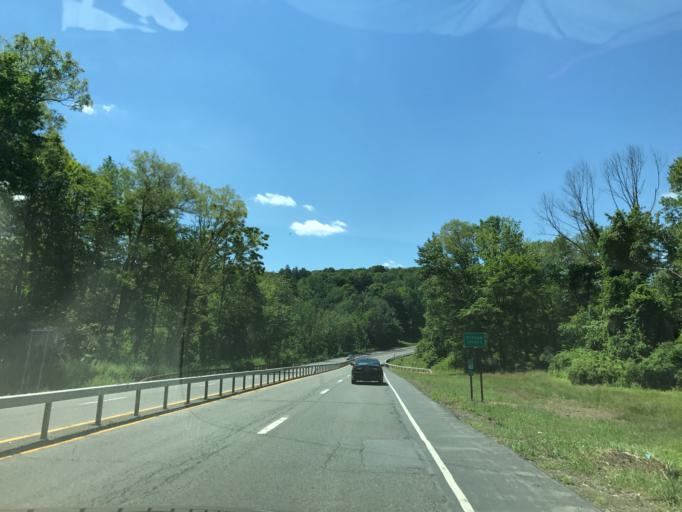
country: US
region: New York
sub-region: Dutchess County
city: Brinckerhoff
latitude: 41.5026
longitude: -73.7956
